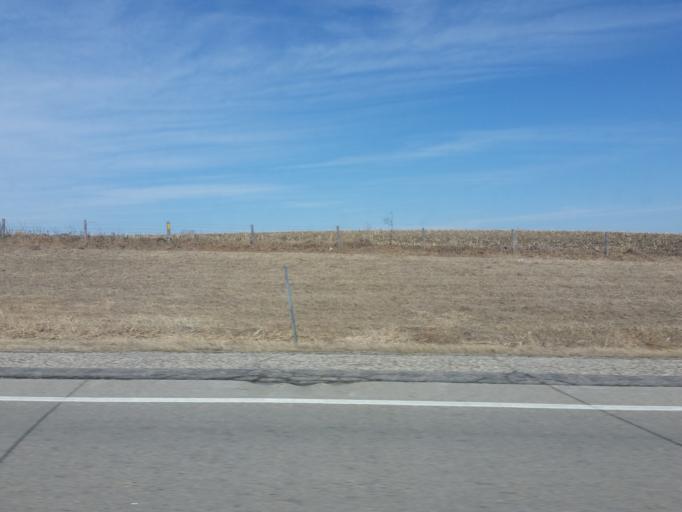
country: US
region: Minnesota
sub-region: Otter Tail County
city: Fergus Falls
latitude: 46.3571
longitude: -96.1553
